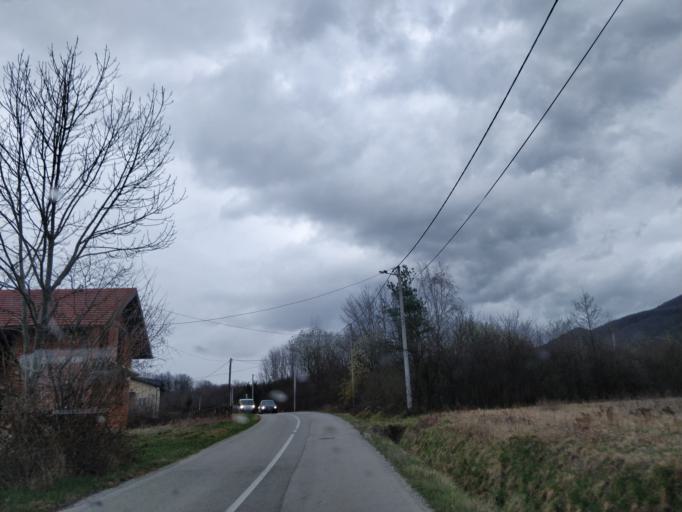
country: HR
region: Zagrebacka
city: Jakovlje
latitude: 45.9242
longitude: 15.9020
